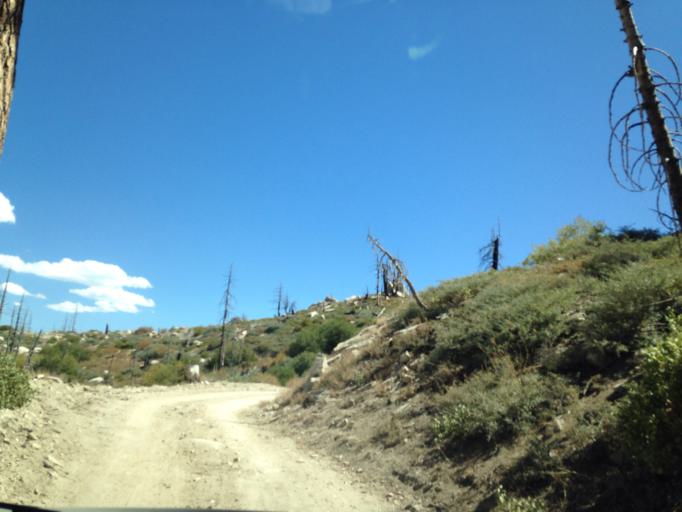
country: US
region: California
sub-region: San Bernardino County
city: Big Bear Lake
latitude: 34.2608
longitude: -116.9930
